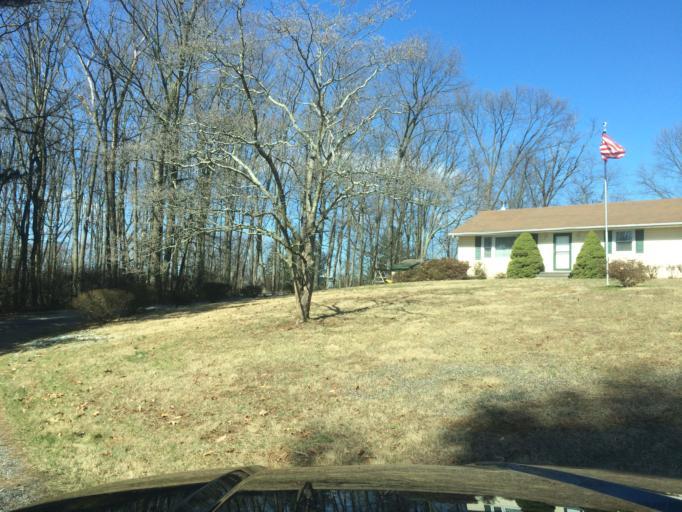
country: US
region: Maryland
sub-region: Carroll County
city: Eldersburg
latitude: 39.4508
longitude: -76.9951
